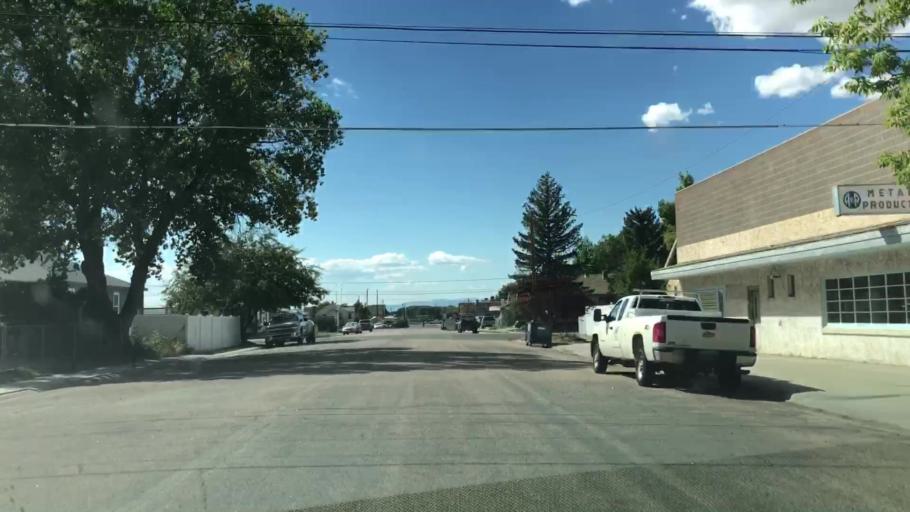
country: US
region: Wyoming
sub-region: Albany County
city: Laramie
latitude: 41.3024
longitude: -105.5924
